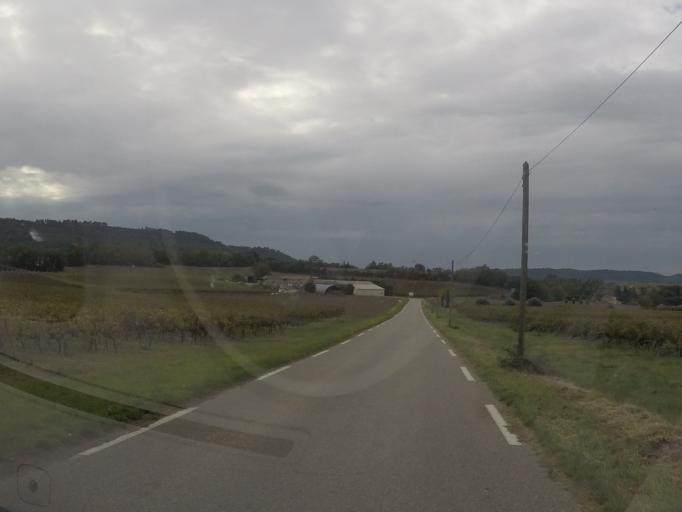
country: FR
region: Provence-Alpes-Cote d'Azur
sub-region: Departement du Vaucluse
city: Ansouis
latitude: 43.7442
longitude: 5.4822
